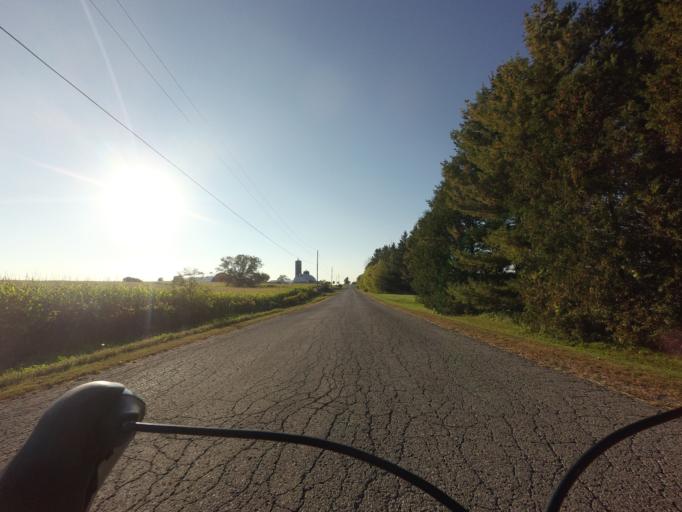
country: CA
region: Ontario
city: Bells Corners
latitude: 45.2251
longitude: -75.7218
